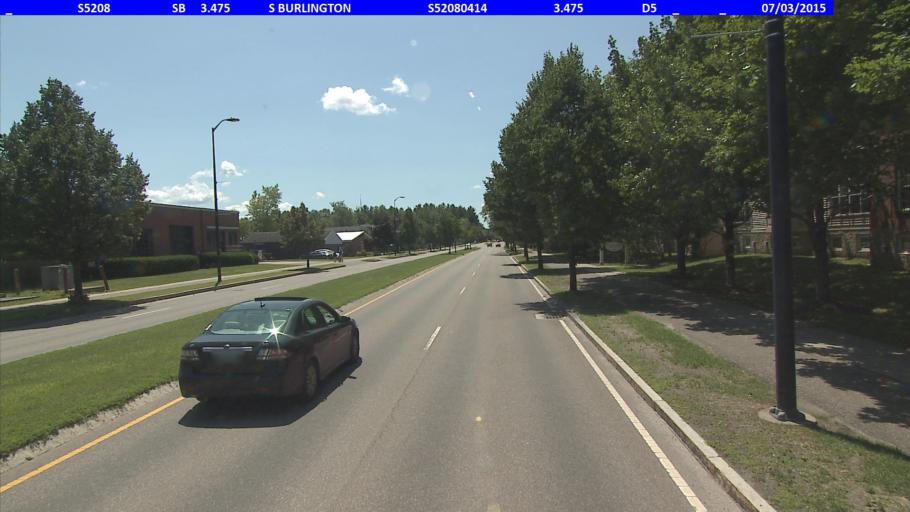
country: US
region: Vermont
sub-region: Chittenden County
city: South Burlington
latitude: 44.4602
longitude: -73.1801
